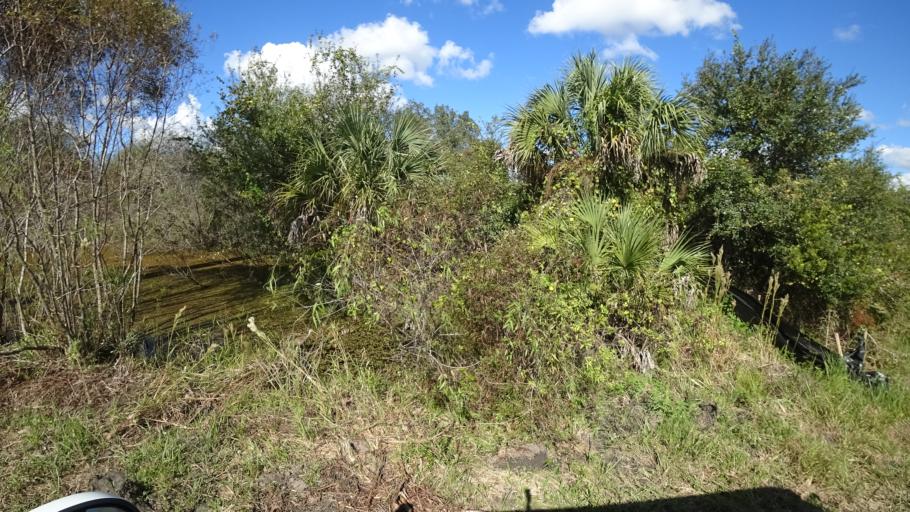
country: US
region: Florida
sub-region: Sarasota County
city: Lake Sarasota
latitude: 27.2484
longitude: -82.2866
